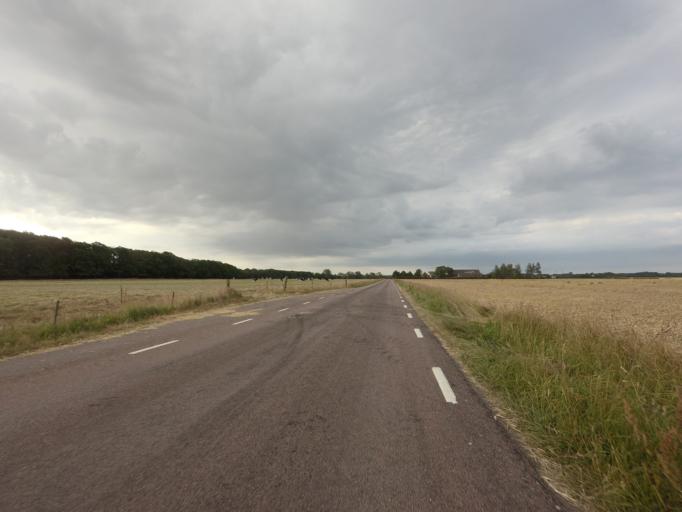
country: SE
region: Skane
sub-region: Helsingborg
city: Odakra
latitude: 56.1510
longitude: 12.7312
